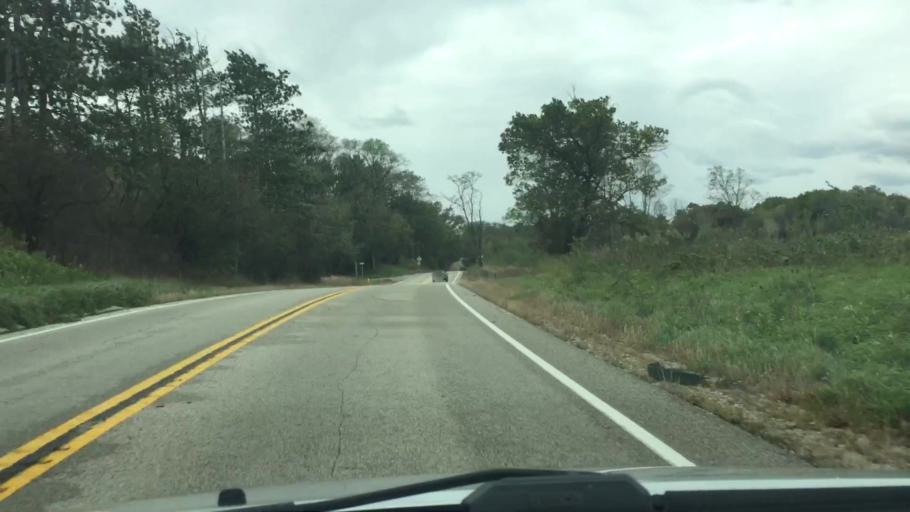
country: US
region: Wisconsin
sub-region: Waukesha County
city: Eagle
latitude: 42.9273
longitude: -88.4664
